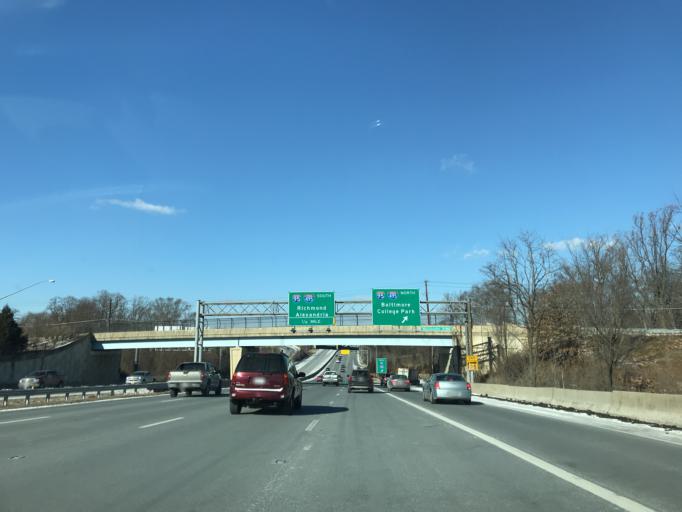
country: US
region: Maryland
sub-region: Prince George's County
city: Camp Springs
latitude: 38.8156
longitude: -76.9146
